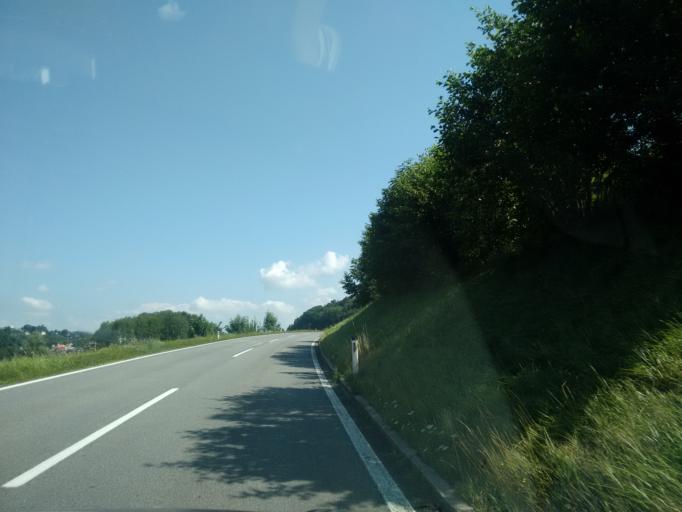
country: AT
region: Upper Austria
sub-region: Politischer Bezirk Kirchdorf an der Krems
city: Kremsmunster
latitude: 48.0392
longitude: 14.1244
